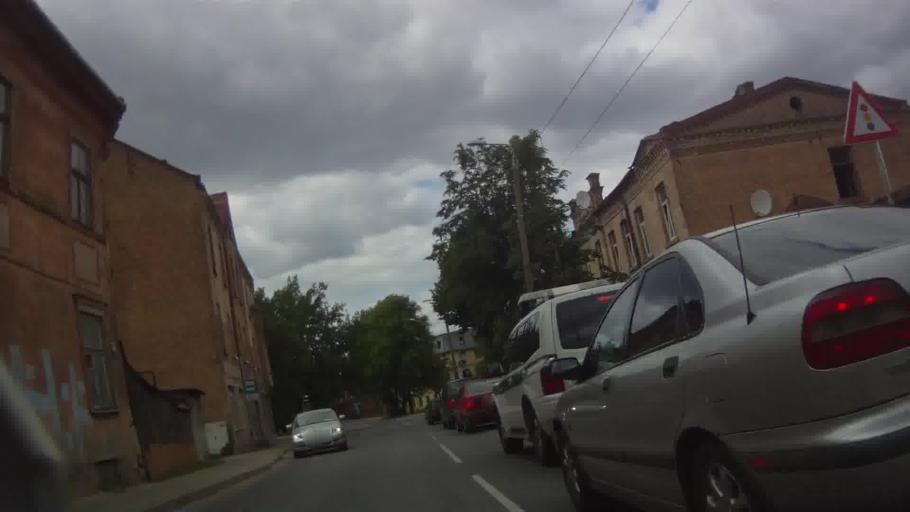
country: LV
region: Kekava
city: Balozi
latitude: 56.9138
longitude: 24.1418
